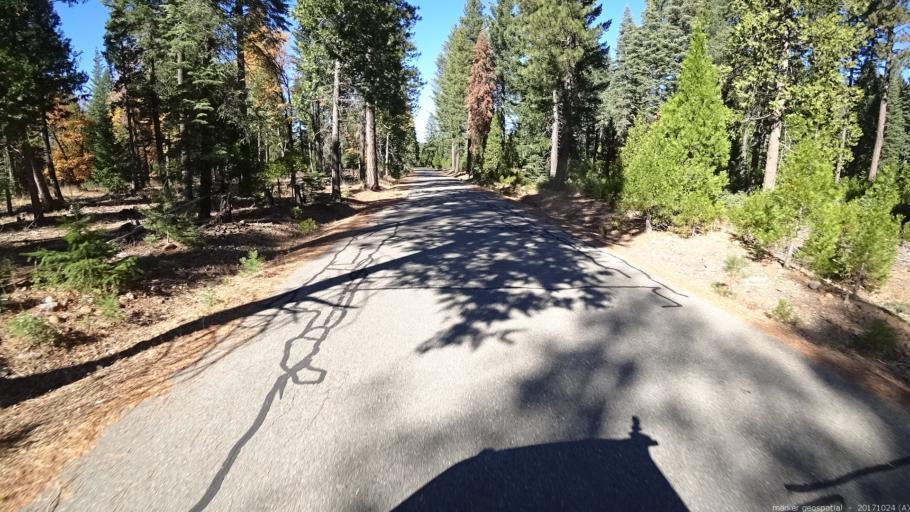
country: US
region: California
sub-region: Shasta County
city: Shingletown
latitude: 40.5079
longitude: -121.6674
